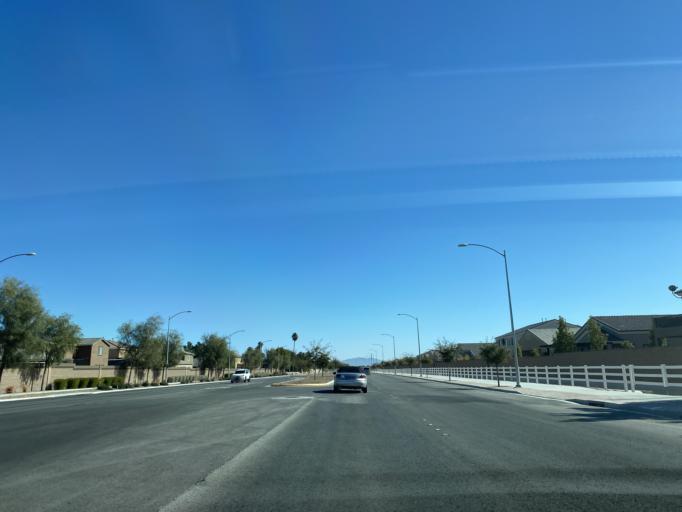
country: US
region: Nevada
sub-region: Clark County
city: North Las Vegas
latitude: 36.3051
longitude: -115.2560
